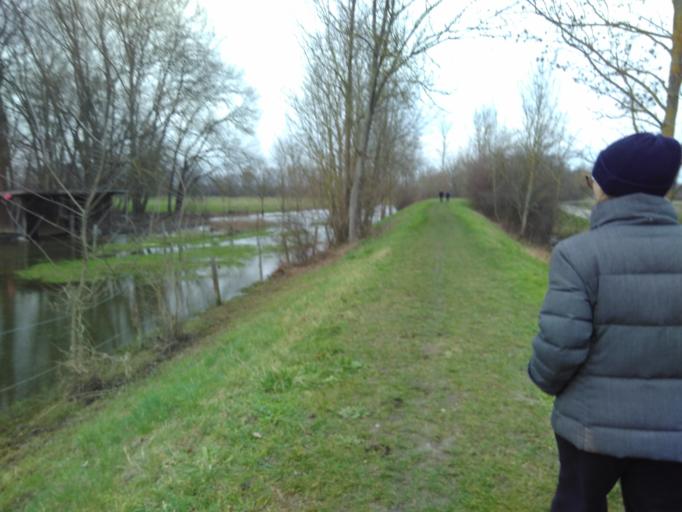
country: FR
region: Alsace
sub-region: Departement du Bas-Rhin
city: Muttersholtz
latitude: 48.2692
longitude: 7.5269
